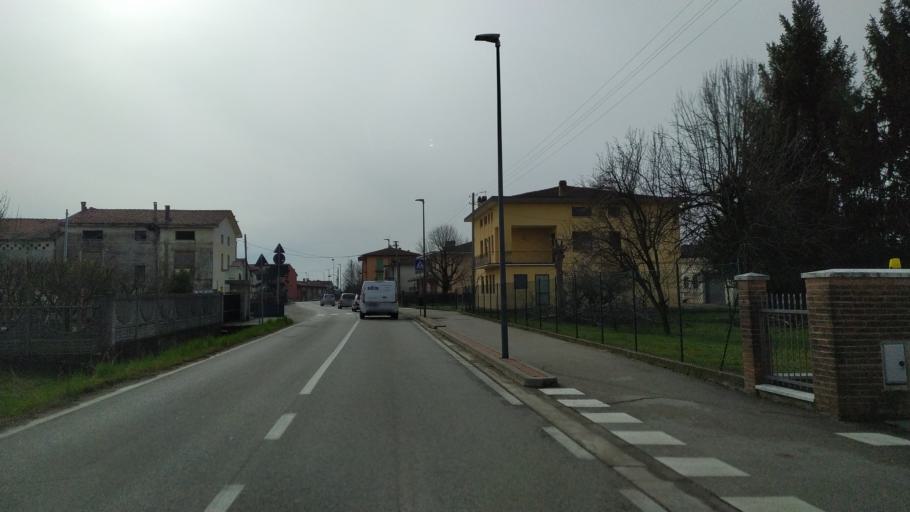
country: IT
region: Veneto
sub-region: Provincia di Vicenza
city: Novoledo
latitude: 45.6460
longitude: 11.5036
